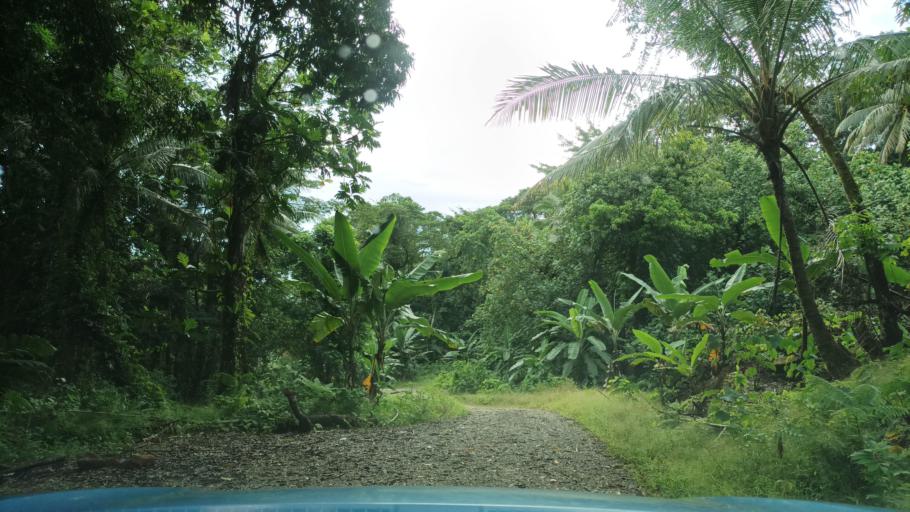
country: FM
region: Pohnpei
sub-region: Sokehs Municipality
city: Palikir - National Government Center
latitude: 6.8822
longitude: 158.1749
